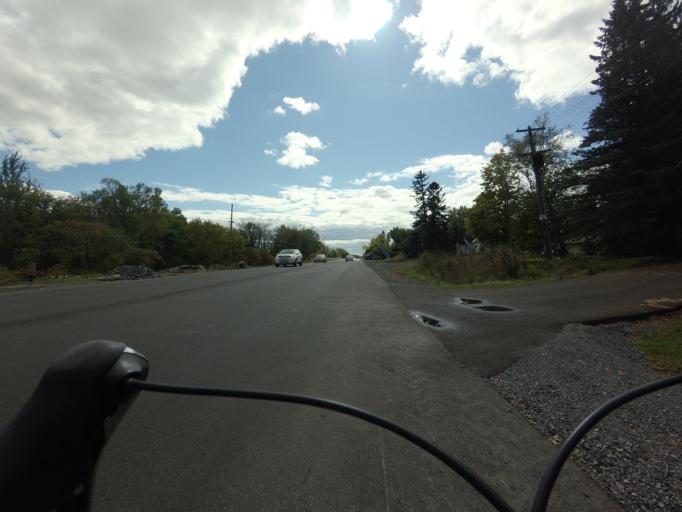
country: CA
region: Ontario
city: Ottawa
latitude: 45.3005
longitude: -75.7011
